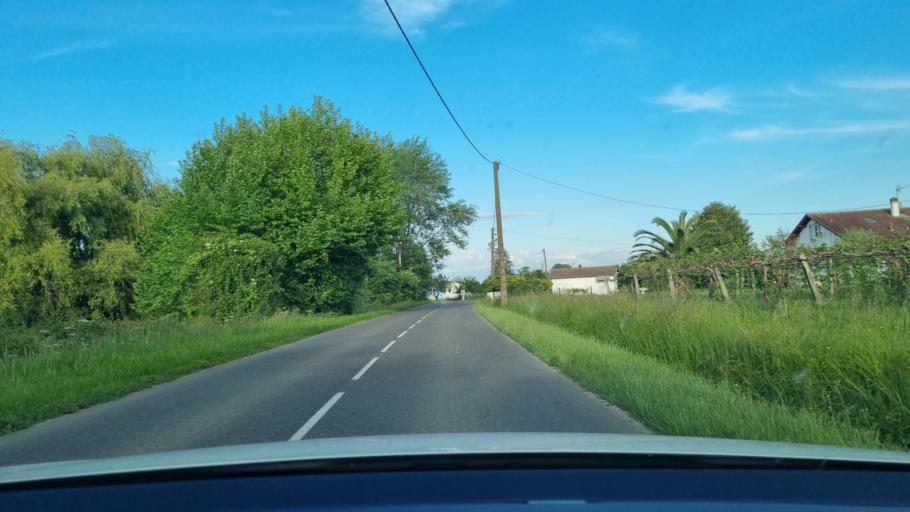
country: FR
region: Aquitaine
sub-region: Departement des Landes
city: Peyrehorade
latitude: 43.5417
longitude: -1.1384
